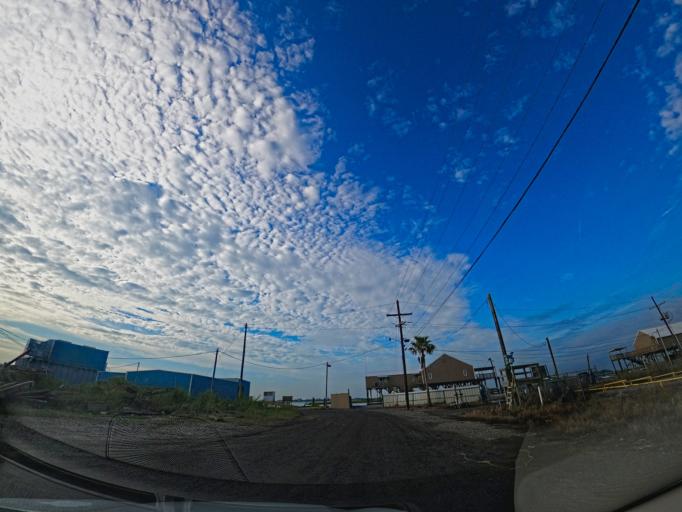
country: US
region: Louisiana
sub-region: Terrebonne Parish
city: Dulac
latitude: 29.2459
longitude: -90.6624
